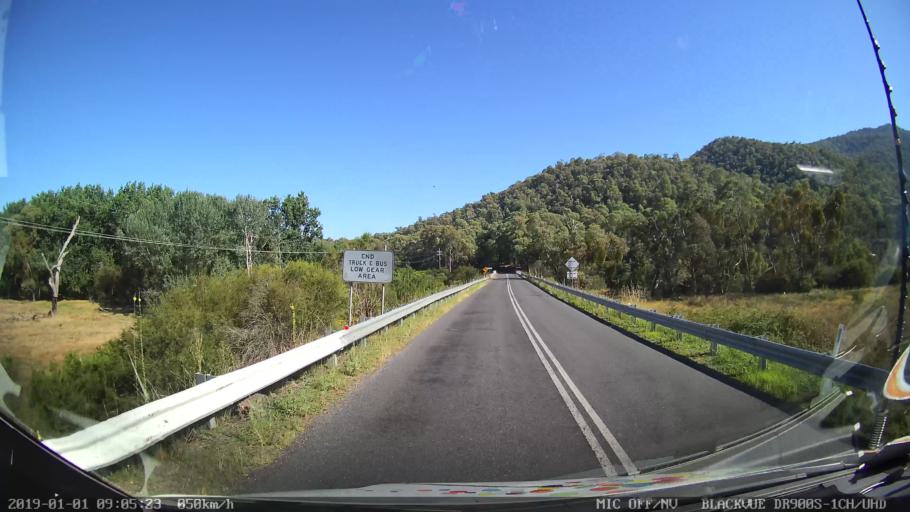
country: AU
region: New South Wales
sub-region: Snowy River
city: Jindabyne
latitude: -36.2201
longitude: 148.1467
